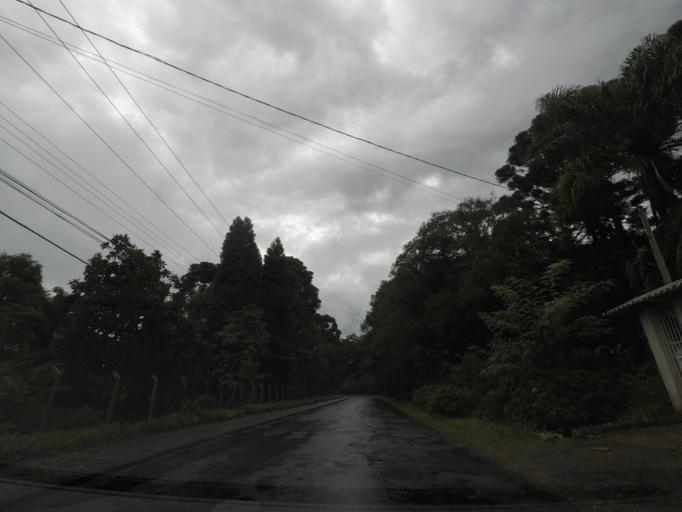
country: BR
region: Parana
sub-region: Campo Largo
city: Campo Largo
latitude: -25.4517
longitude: -49.4471
